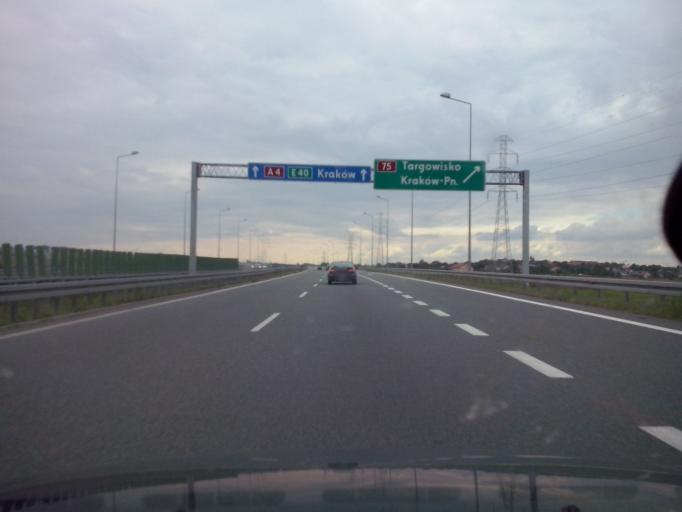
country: PL
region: Lesser Poland Voivodeship
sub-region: Powiat wielicki
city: Szarow
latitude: 49.9905
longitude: 20.2804
